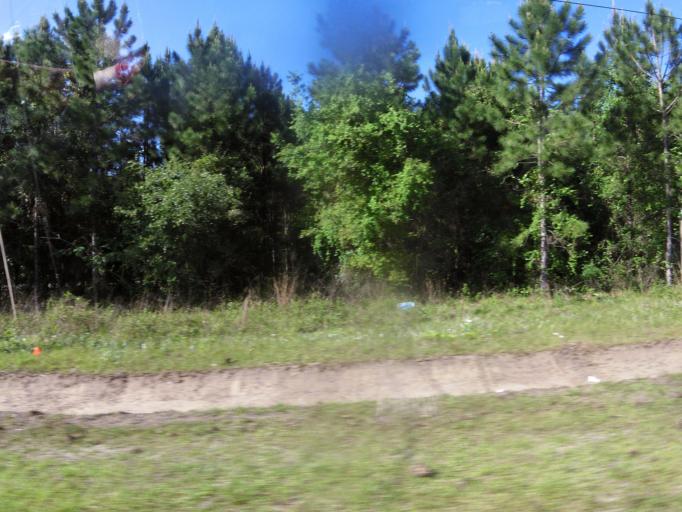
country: US
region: Florida
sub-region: Duval County
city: Jacksonville
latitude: 30.4347
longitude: -81.5667
